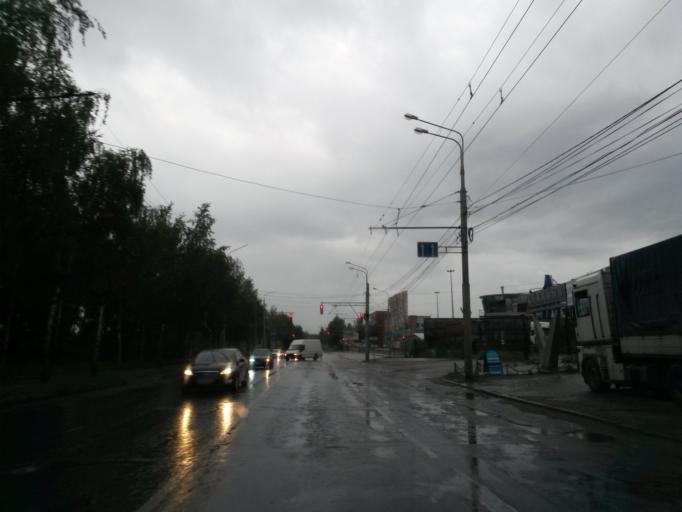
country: RU
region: Jaroslavl
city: Yaroslavl
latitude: 57.6564
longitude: 39.8671
